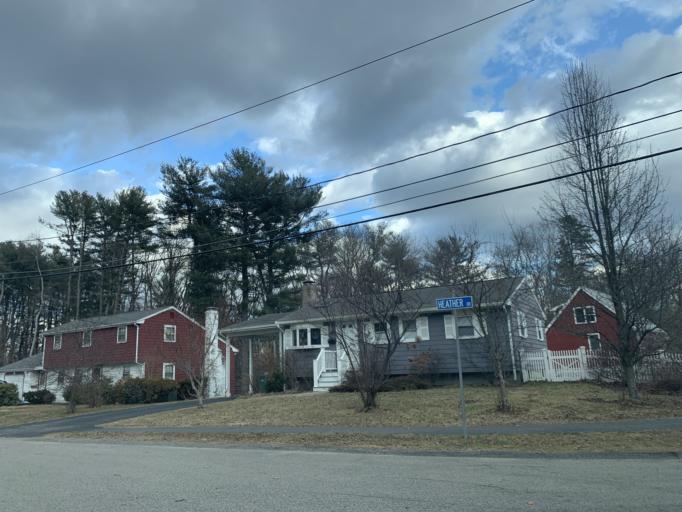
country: US
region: Massachusetts
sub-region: Norfolk County
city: Norwood
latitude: 42.1775
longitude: -71.1746
